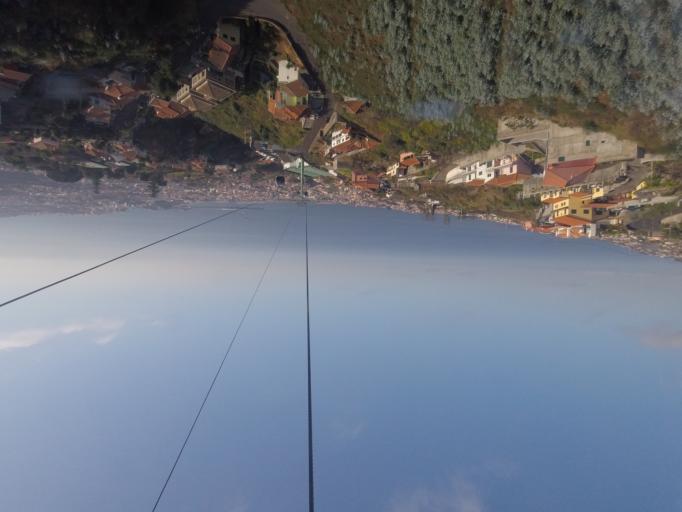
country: PT
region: Madeira
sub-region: Funchal
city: Nossa Senhora do Monte
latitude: 32.6724
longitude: -16.9004
